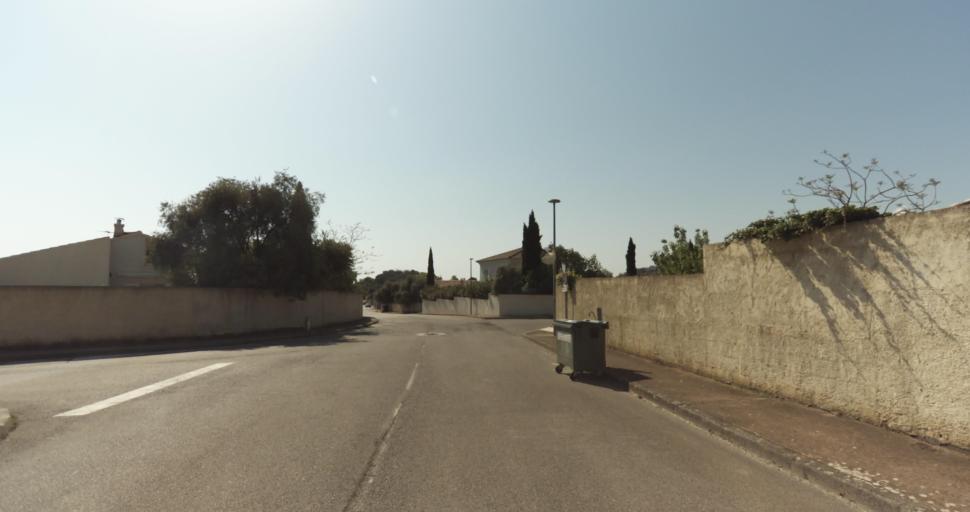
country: FR
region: Corsica
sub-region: Departement de la Haute-Corse
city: Biguglia
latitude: 42.6261
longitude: 9.4261
